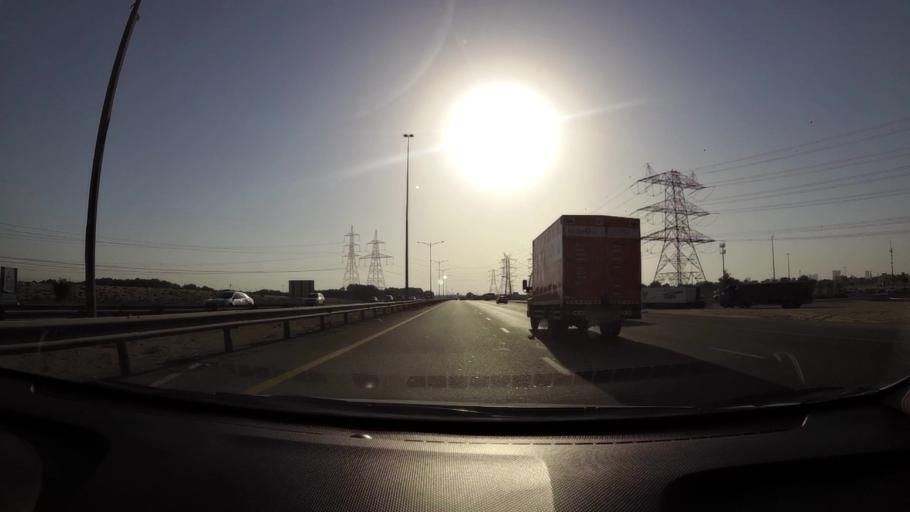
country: AE
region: Ajman
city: Ajman
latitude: 25.3581
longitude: 55.4949
